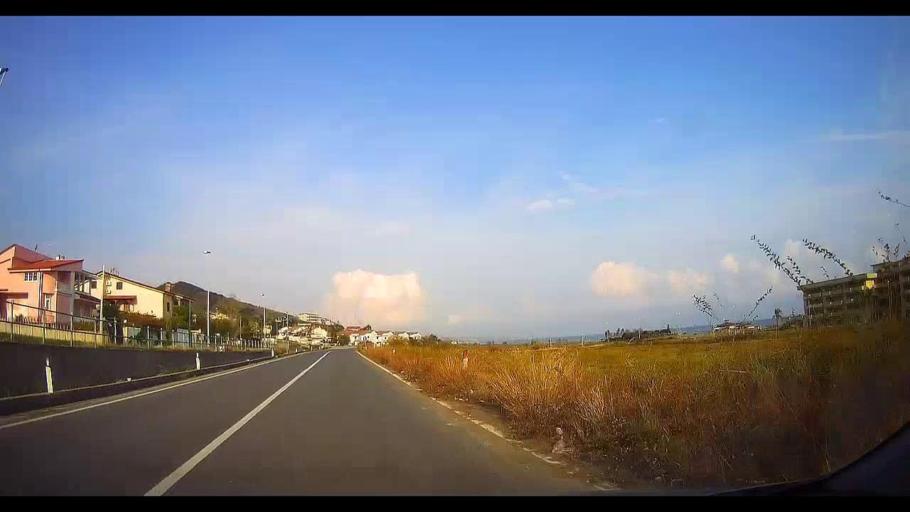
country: IT
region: Calabria
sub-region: Provincia di Cosenza
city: Cariati
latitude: 39.5256
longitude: 16.8907
